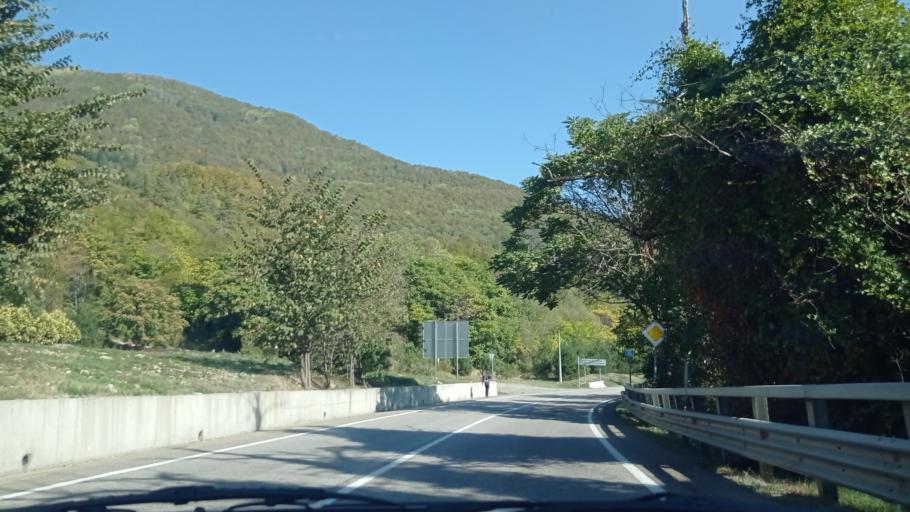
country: RU
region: Krasnodarskiy
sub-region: Sochi City
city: Krasnaya Polyana
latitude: 43.6848
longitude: 40.2277
